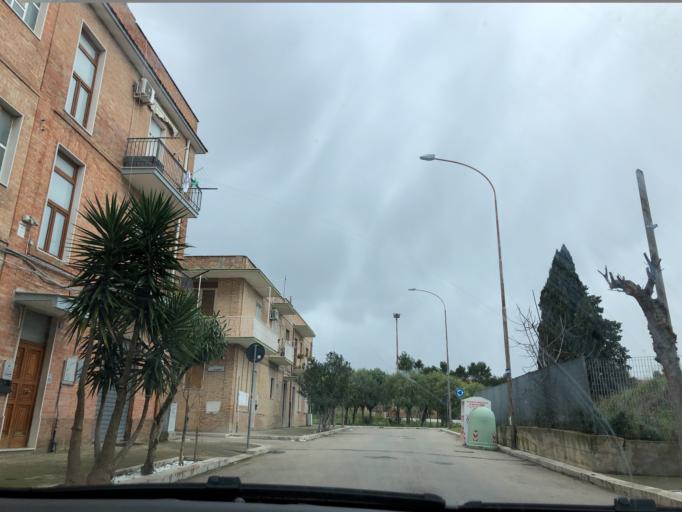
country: IT
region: Apulia
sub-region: Provincia di Foggia
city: Lucera
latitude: 41.5083
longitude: 15.3250
